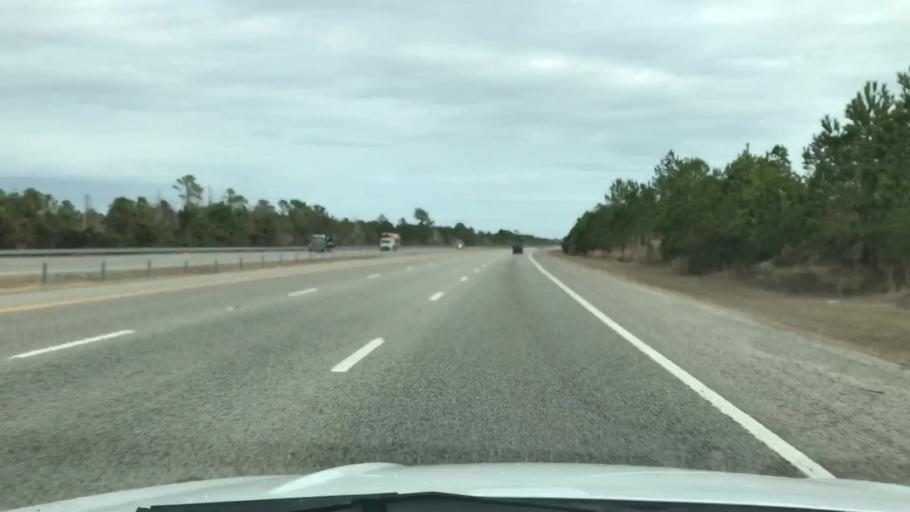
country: US
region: South Carolina
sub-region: Horry County
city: Forestbrook
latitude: 33.7236
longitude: -78.9926
